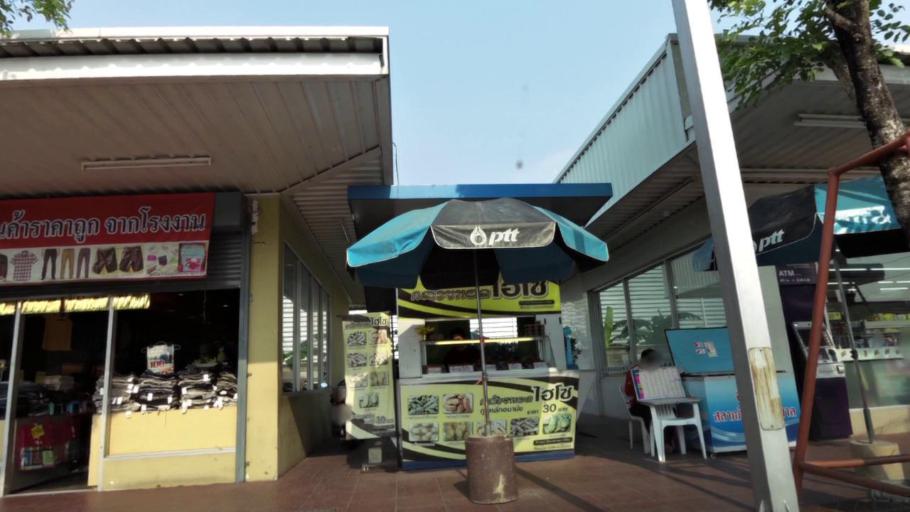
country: TH
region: Phra Nakhon Si Ayutthaya
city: Phra Nakhon Si Ayutthaya
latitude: 14.3249
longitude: 100.6257
